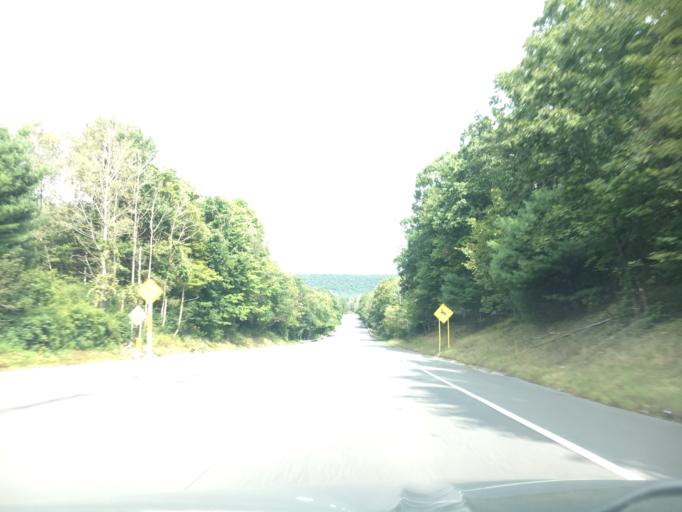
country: US
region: Pennsylvania
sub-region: Schuylkill County
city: Hometown
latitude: 40.8439
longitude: -75.9978
